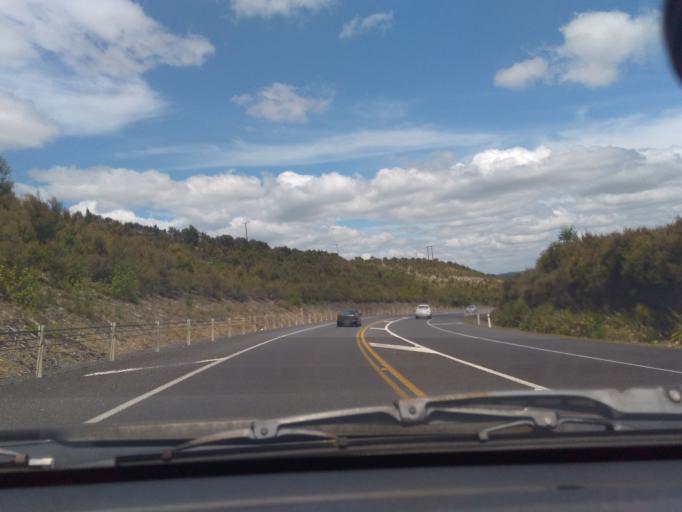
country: NZ
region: Northland
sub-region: Far North District
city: Kerikeri
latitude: -35.2721
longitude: 173.9475
